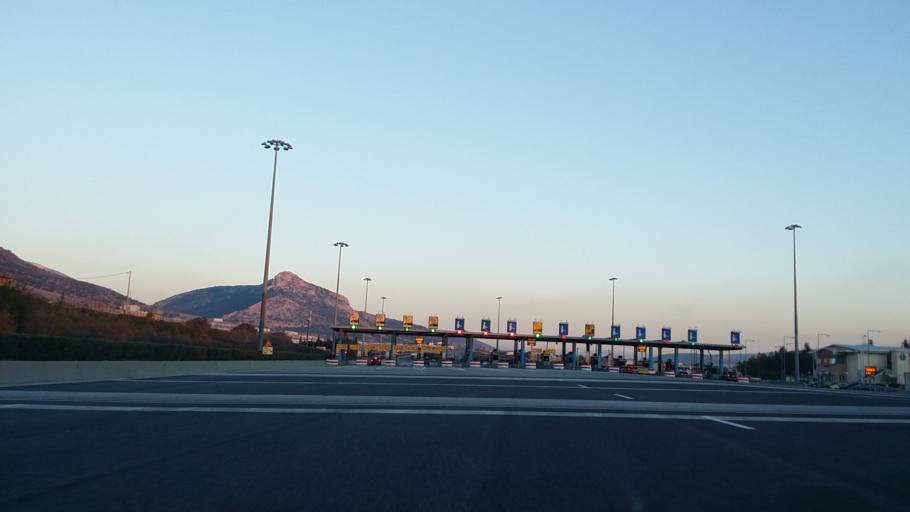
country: GR
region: Attica
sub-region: Nomarchia Dytikis Attikis
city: Aspropyrgos
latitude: 38.0943
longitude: 23.5892
